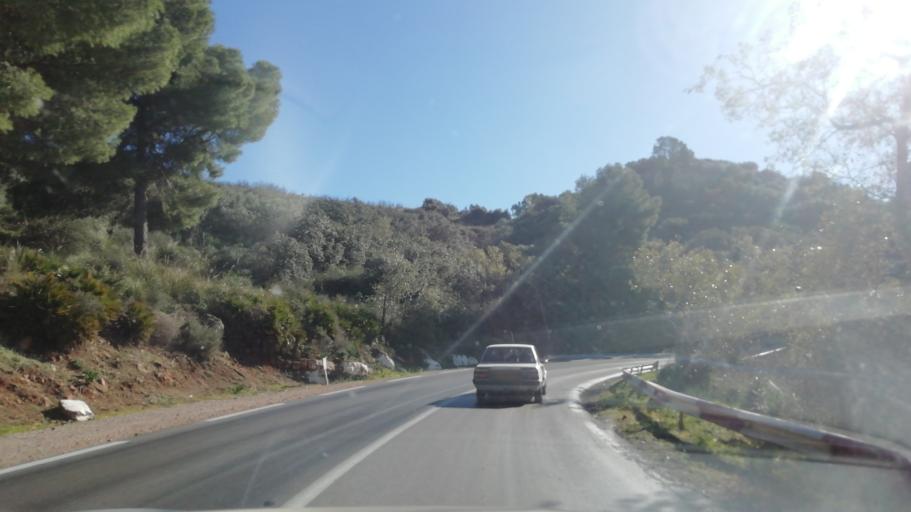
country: DZ
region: Tlemcen
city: Mansoura
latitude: 34.8515
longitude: -1.3520
